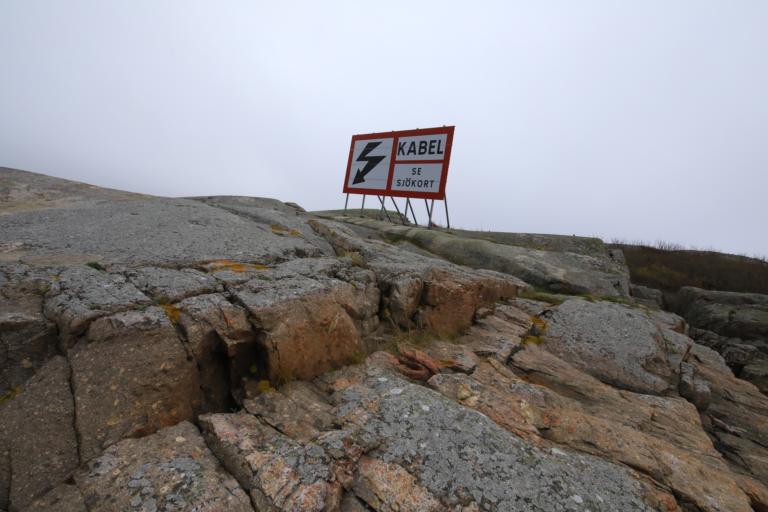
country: SE
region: Vaestra Goetaland
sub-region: Ockero Kommun
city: Hono
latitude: 57.6339
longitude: 11.6115
